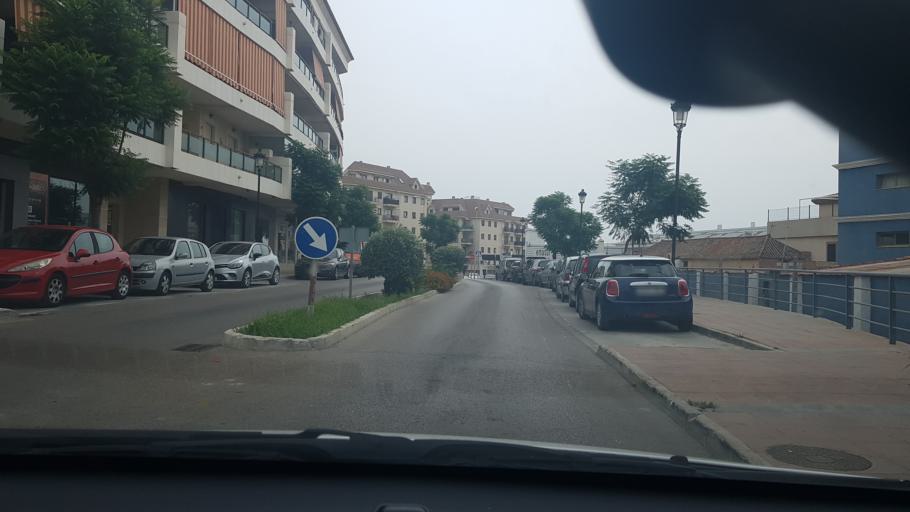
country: ES
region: Andalusia
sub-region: Provincia de Malaga
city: Manilva
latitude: 36.3670
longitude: -5.2291
